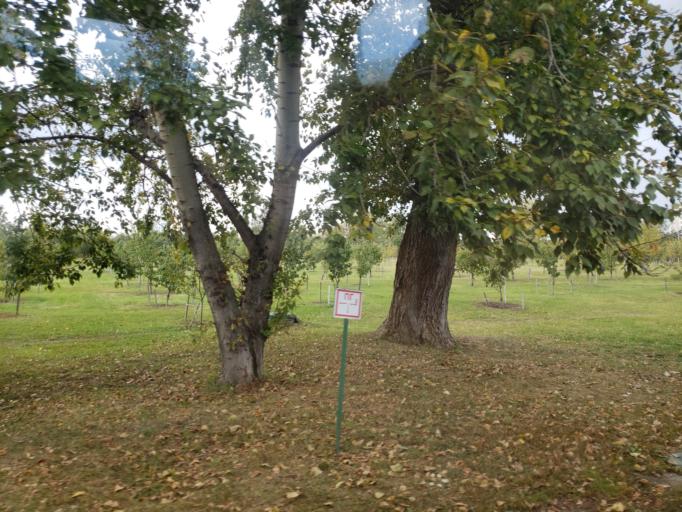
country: RU
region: Moscow
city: Kolomenskoye
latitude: 55.6738
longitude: 37.6758
